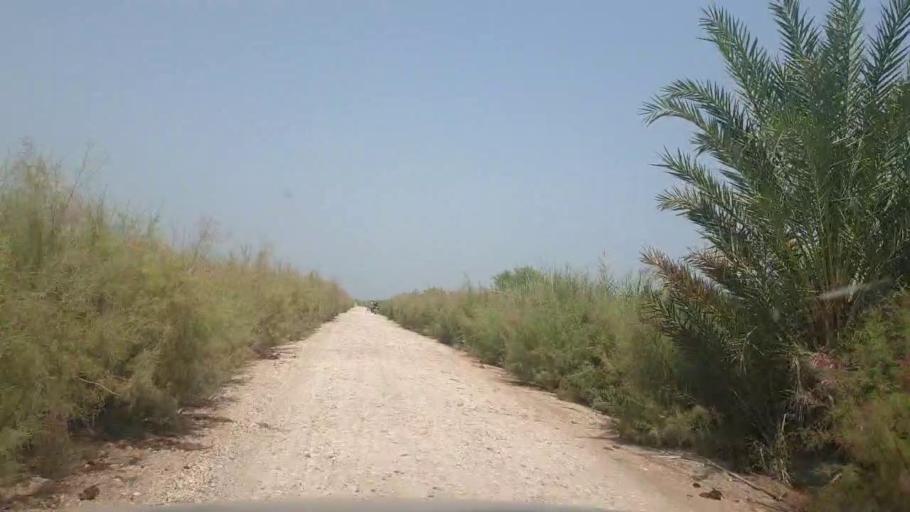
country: PK
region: Sindh
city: Lakhi
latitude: 27.8413
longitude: 68.6268
